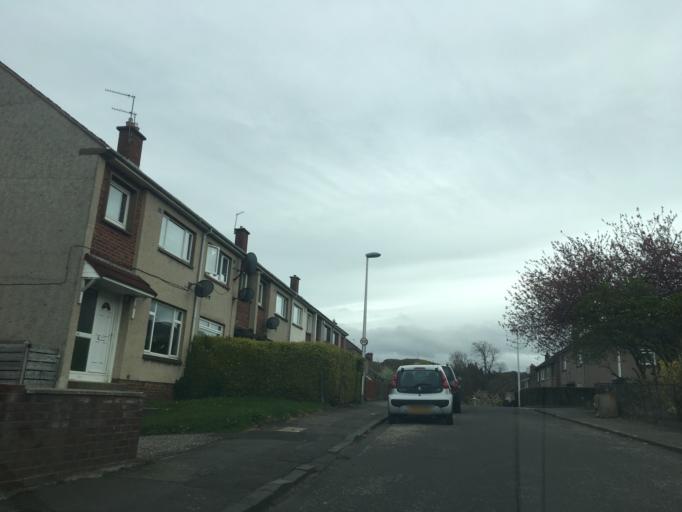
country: GB
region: Scotland
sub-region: Edinburgh
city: Colinton
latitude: 55.9242
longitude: -3.2549
